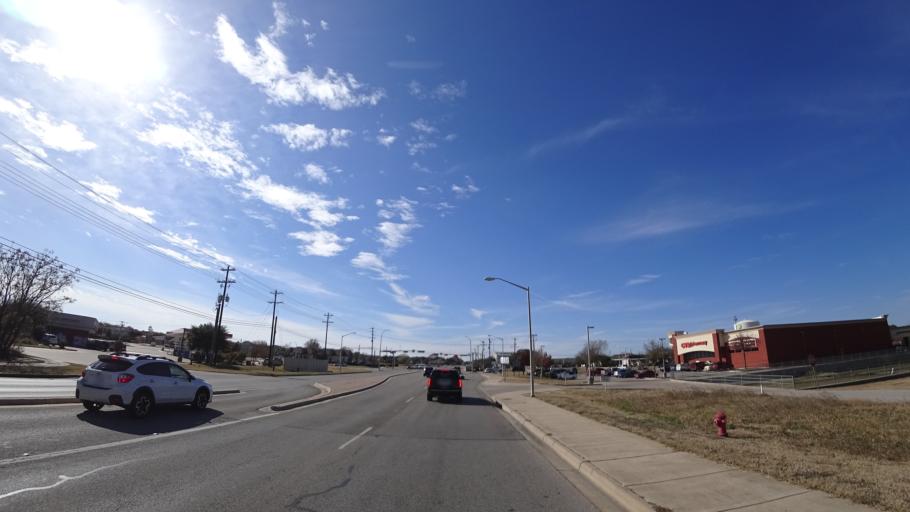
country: US
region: Texas
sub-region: Williamson County
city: Cedar Park
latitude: 30.5303
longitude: -97.8437
